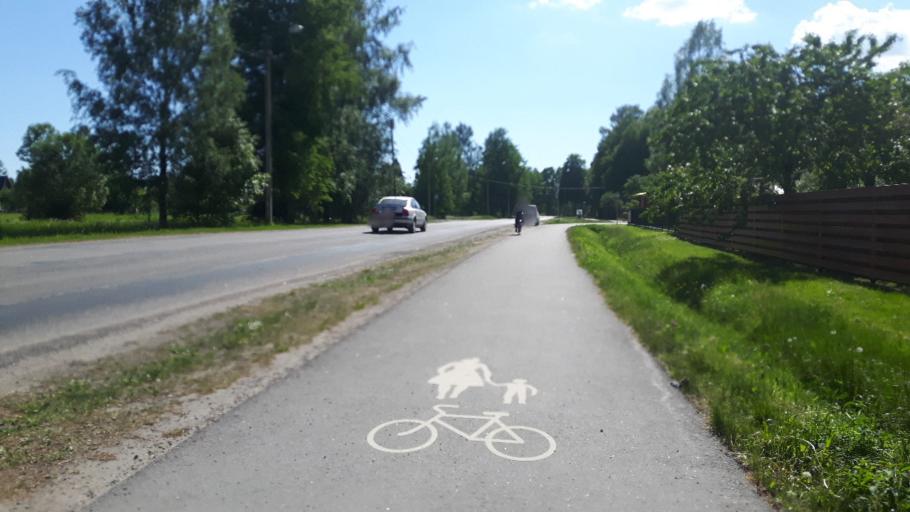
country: EE
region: Paernumaa
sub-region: Paikuse vald
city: Paikuse
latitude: 58.3988
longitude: 24.6447
